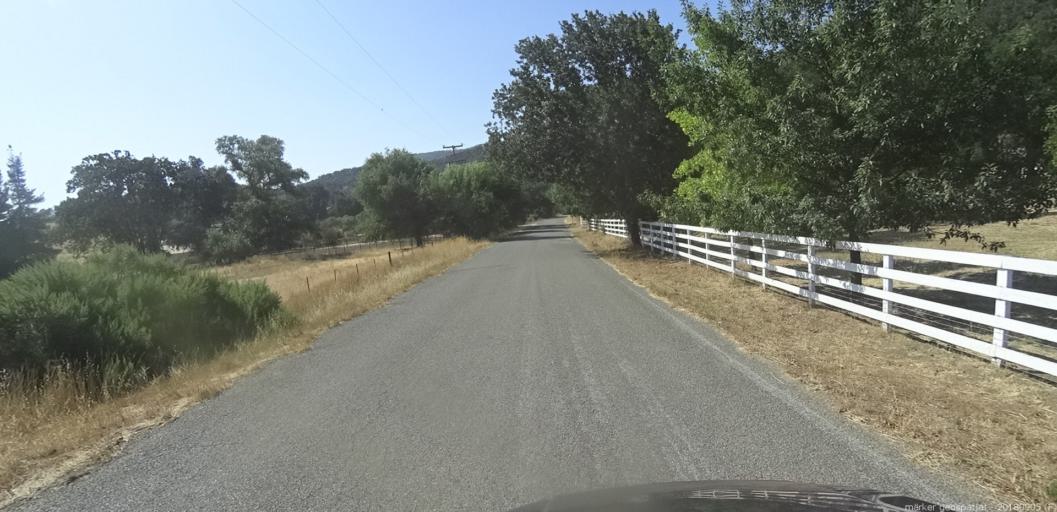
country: US
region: California
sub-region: Monterey County
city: Gonzales
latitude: 36.3988
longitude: -121.5803
